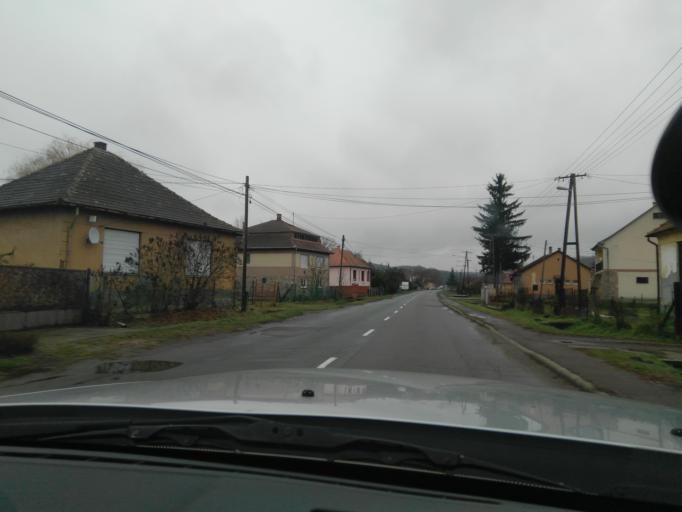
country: HU
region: Nograd
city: Matraterenye
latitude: 48.0284
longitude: 19.9500
